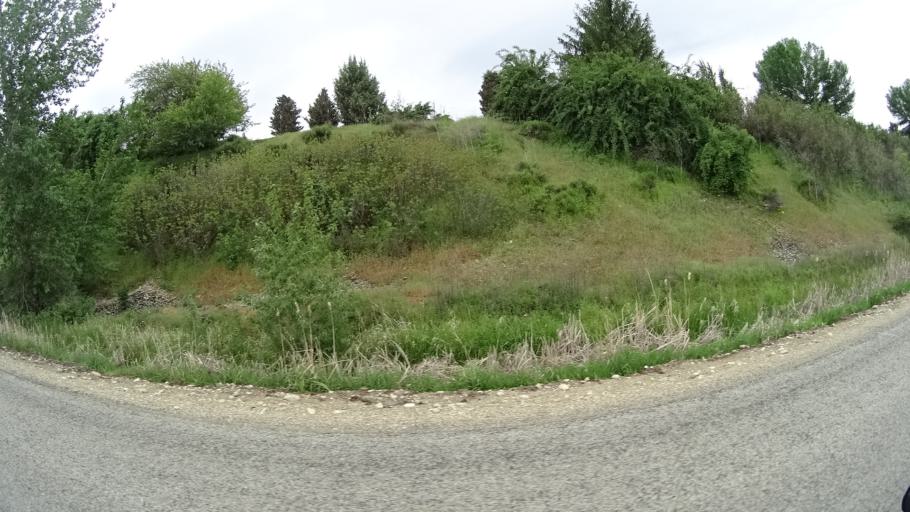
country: US
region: Idaho
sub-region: Ada County
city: Star
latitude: 43.6699
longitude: -116.4753
